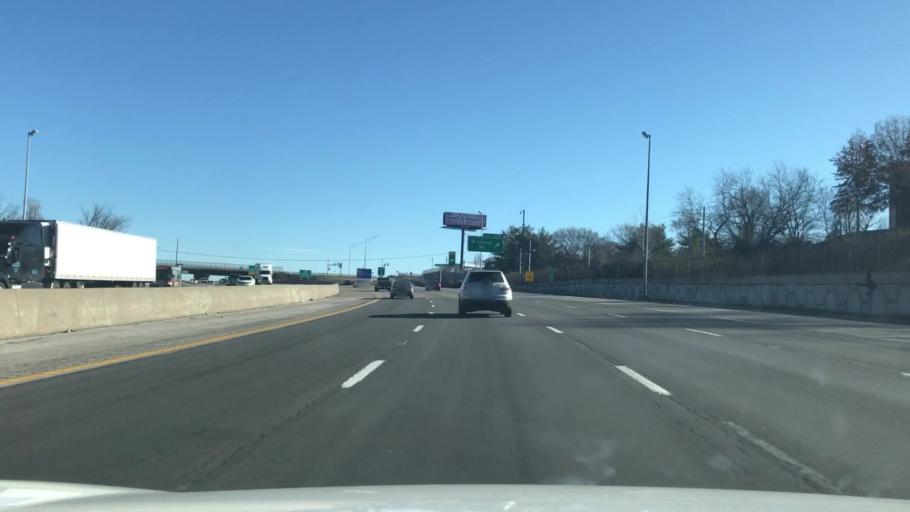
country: US
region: Missouri
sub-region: Saint Louis County
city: Cool Valley
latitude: 38.7215
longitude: -90.3210
